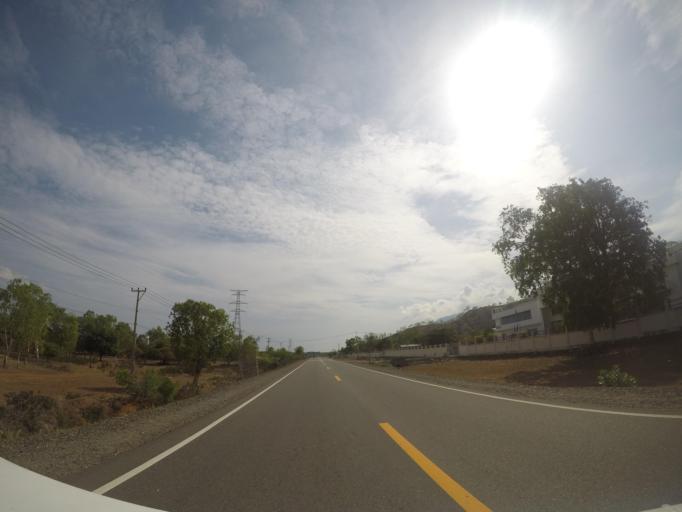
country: ID
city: Metinaro
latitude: -8.5147
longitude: 125.7805
